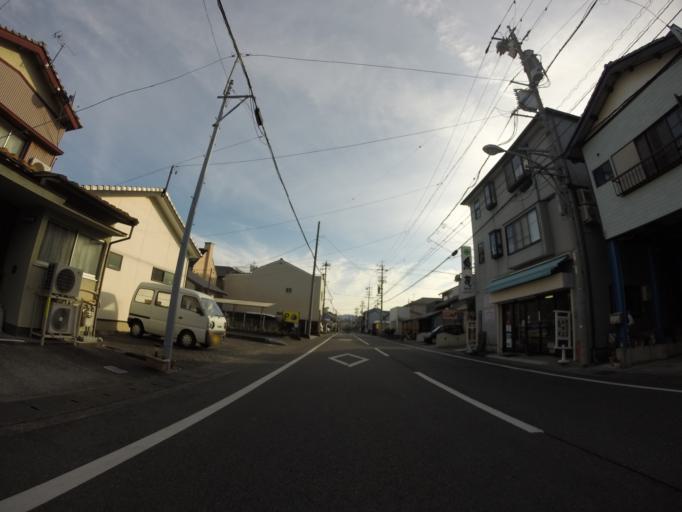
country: JP
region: Shizuoka
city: Shizuoka-shi
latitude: 35.0312
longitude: 138.4829
